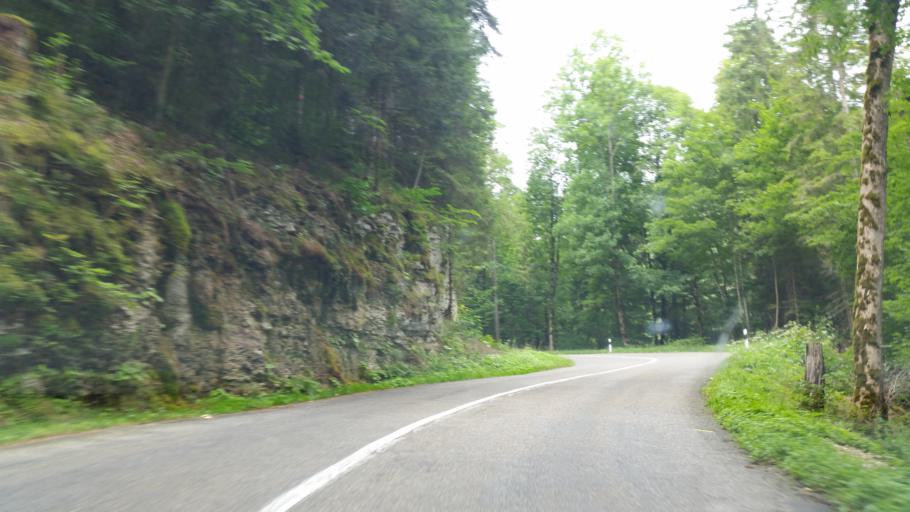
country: CH
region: Neuchatel
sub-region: La Chaux-de-Fonds District
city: La Chaux-de-Fonds
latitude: 47.1483
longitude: 6.8404
